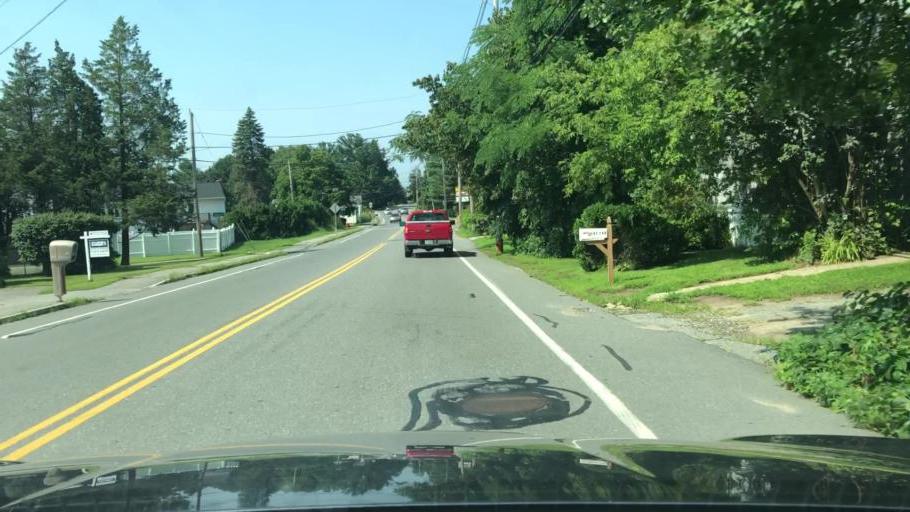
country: US
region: Massachusetts
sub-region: Essex County
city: Methuen
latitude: 42.7500
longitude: -71.1724
